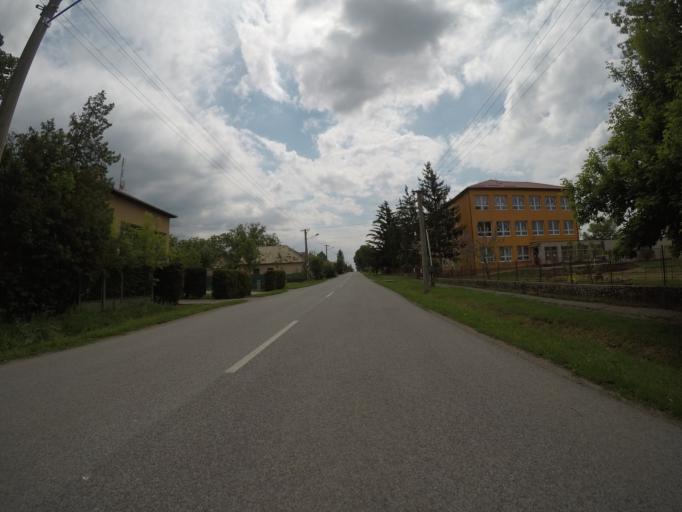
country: SK
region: Nitriansky
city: Zeliezovce
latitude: 48.0193
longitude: 18.7996
